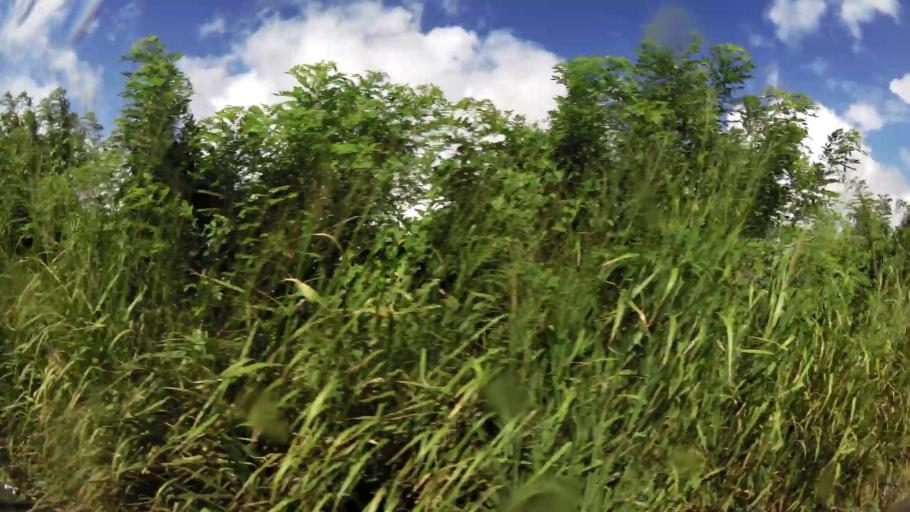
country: MQ
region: Martinique
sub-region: Martinique
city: Saint-Esprit
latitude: 14.5186
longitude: -60.9682
